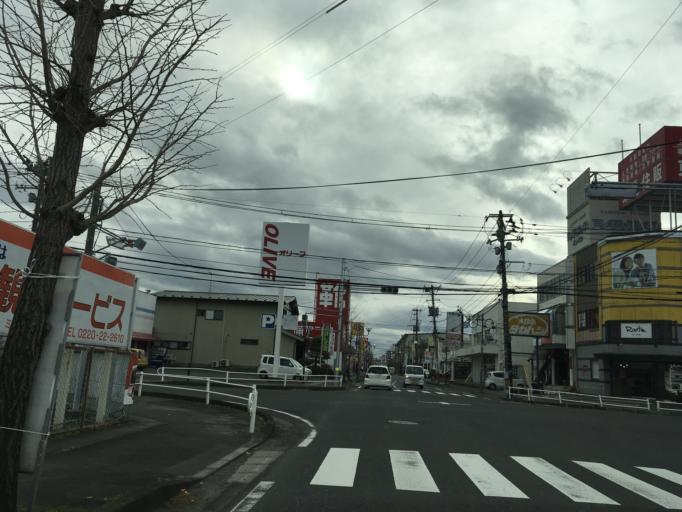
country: JP
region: Miyagi
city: Wakuya
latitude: 38.6901
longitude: 141.1899
